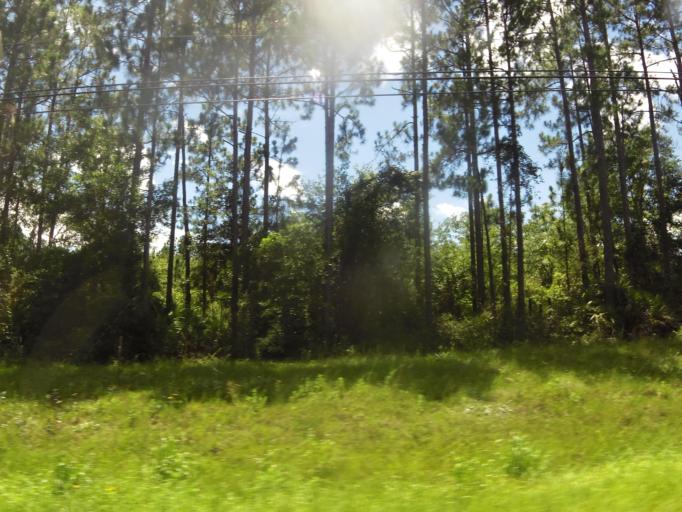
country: US
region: Florida
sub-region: Nassau County
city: Fernandina Beach
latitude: 30.6382
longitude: -81.5298
